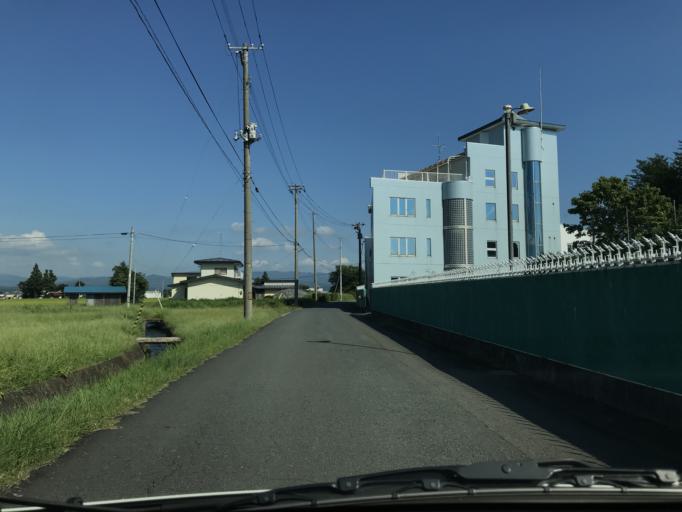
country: JP
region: Iwate
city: Mizusawa
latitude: 39.1599
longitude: 141.1354
